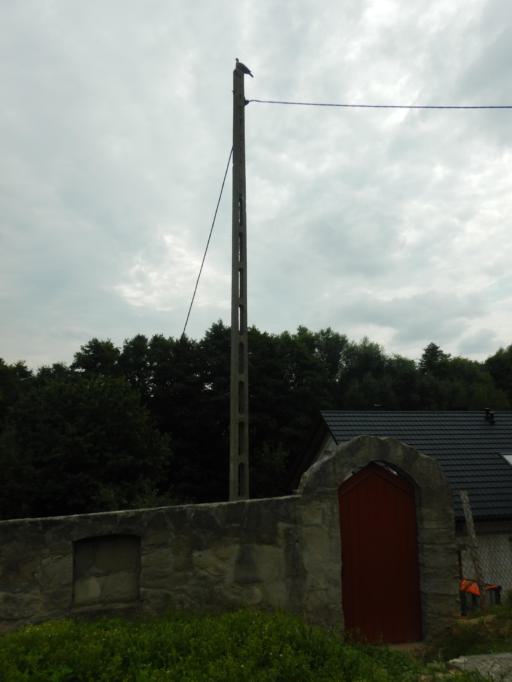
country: PL
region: Swietokrzyskie
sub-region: Powiat opatowski
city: Opatow
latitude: 50.7959
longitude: 21.4324
